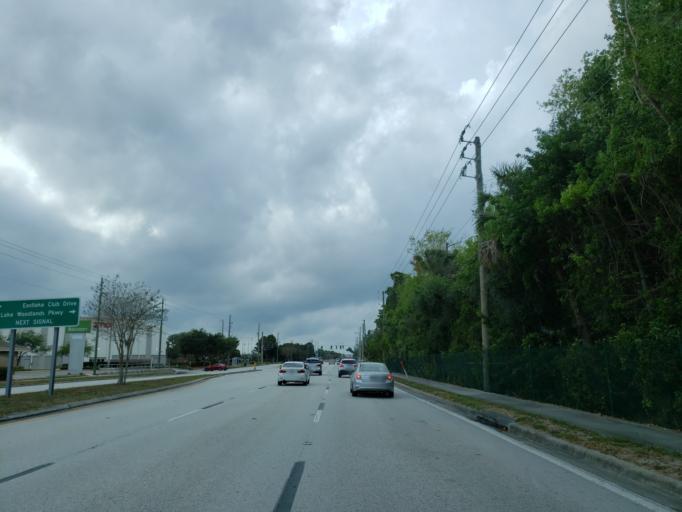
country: US
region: Florida
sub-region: Pinellas County
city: Saint George
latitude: 28.0519
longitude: -82.6982
